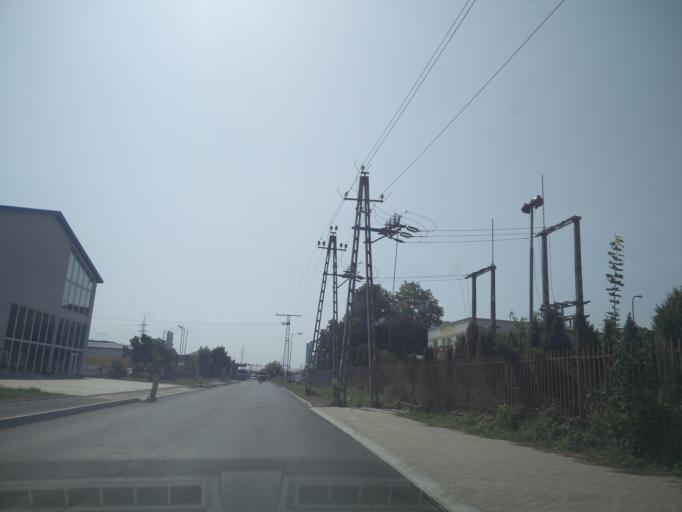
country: HU
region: Zala
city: Zalaegerszeg
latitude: 46.8409
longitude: 16.8624
